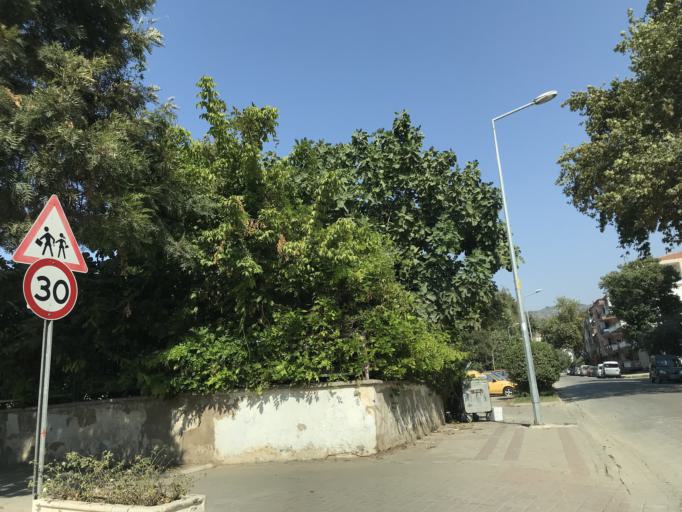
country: TR
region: Izmir
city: Selcuk
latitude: 37.9455
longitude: 27.3693
